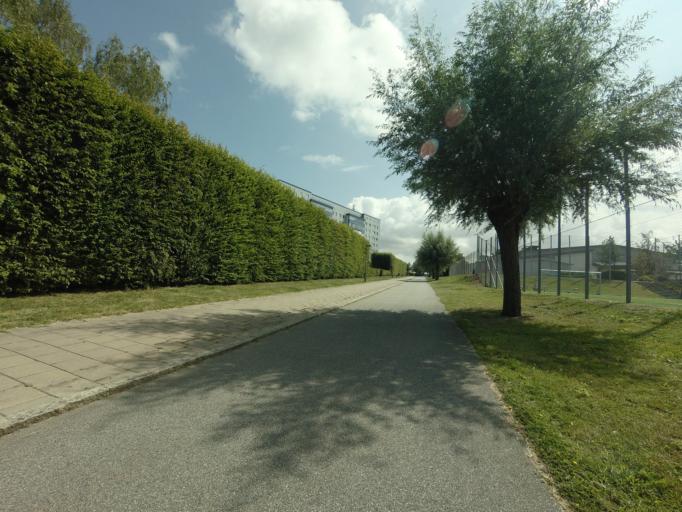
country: SE
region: Skane
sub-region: Malmo
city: Malmoe
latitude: 55.5714
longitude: 13.0002
